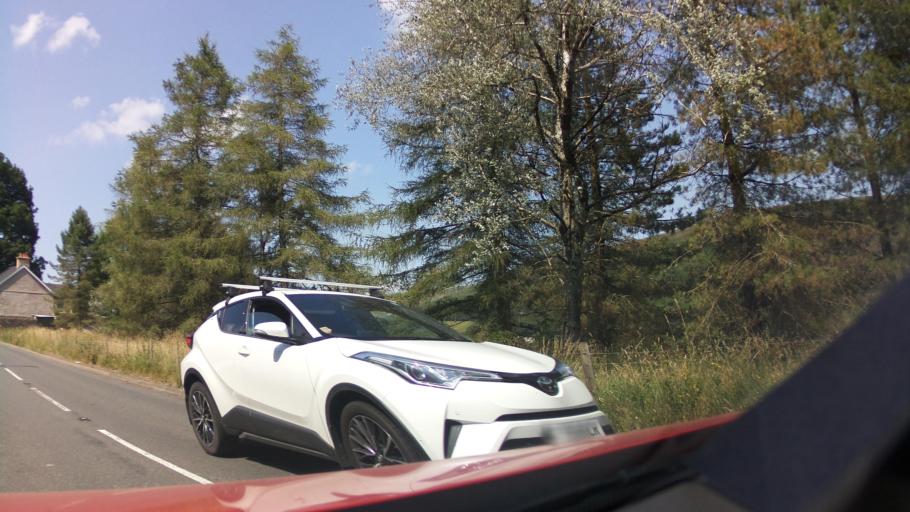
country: GB
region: Wales
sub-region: Caerphilly County Borough
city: New Tredegar
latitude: 51.7317
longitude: -3.2603
